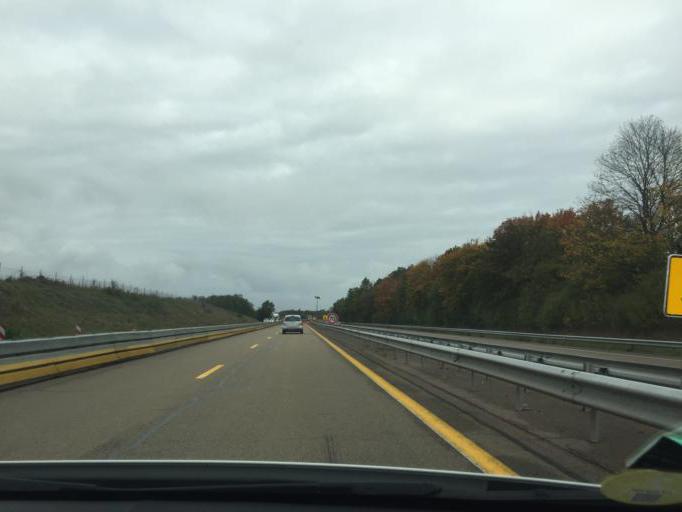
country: FR
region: Centre
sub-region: Departement du Loiret
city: Courtenay
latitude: 47.9969
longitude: 3.1730
